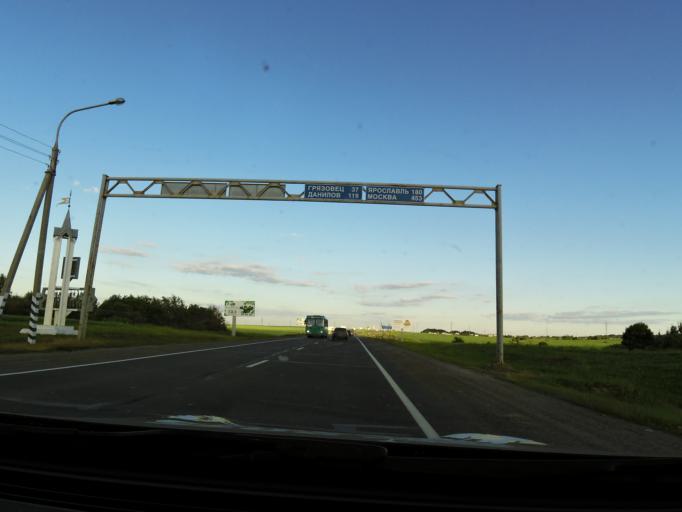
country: RU
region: Vologda
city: Vologda
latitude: 59.1681
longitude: 39.9142
